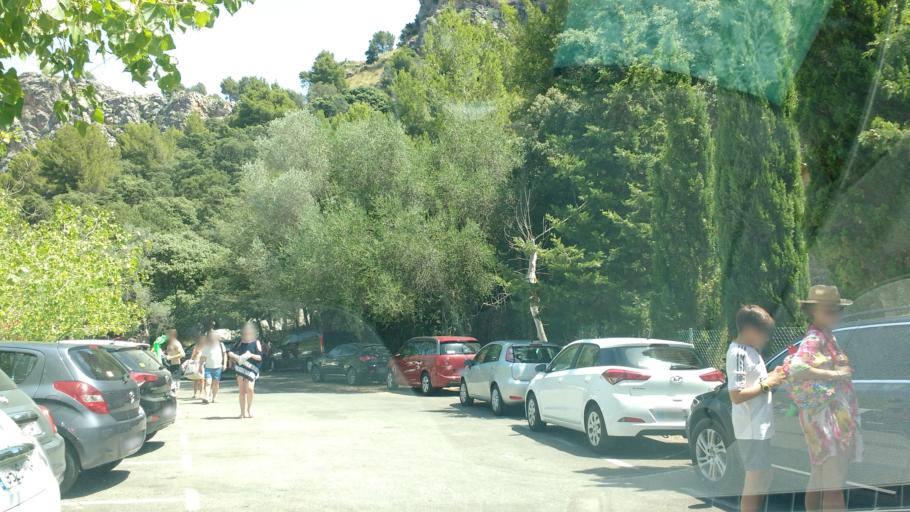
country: ES
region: Balearic Islands
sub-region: Illes Balears
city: Escorca
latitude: 39.8468
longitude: 2.7983
